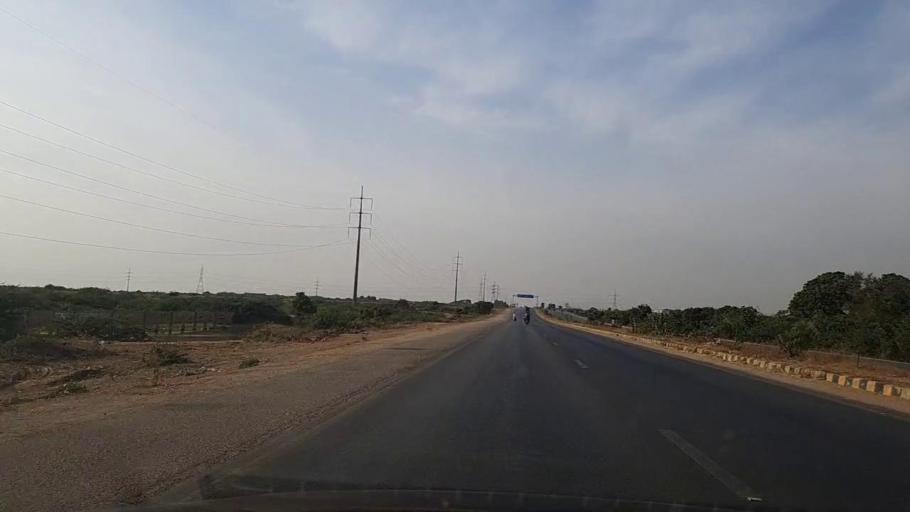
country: PK
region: Sindh
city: Gharo
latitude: 24.7624
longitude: 67.5559
